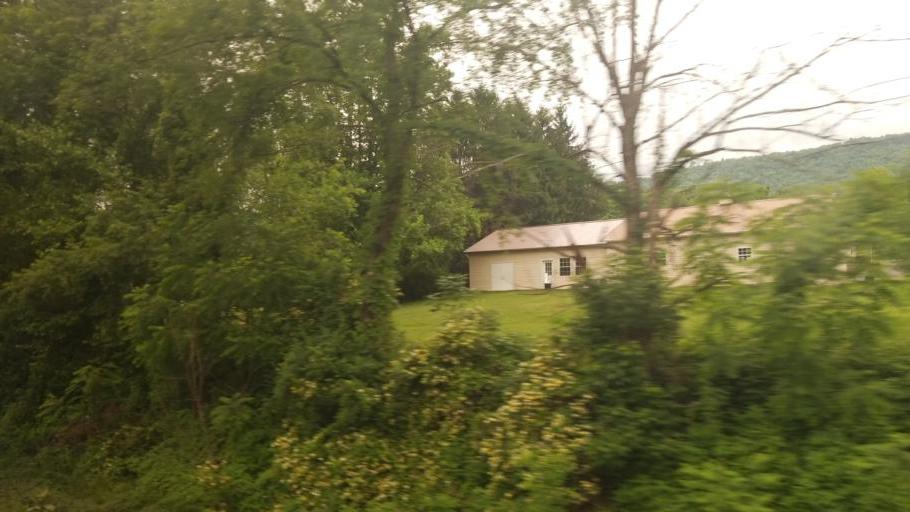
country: US
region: Maryland
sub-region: Allegany County
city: La Vale
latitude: 39.7011
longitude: -78.7844
